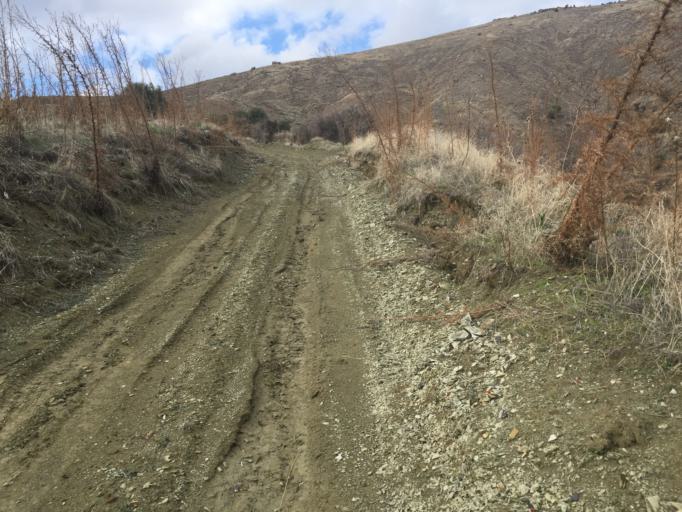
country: CY
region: Limassol
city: Pachna
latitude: 34.8742
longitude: 32.6582
